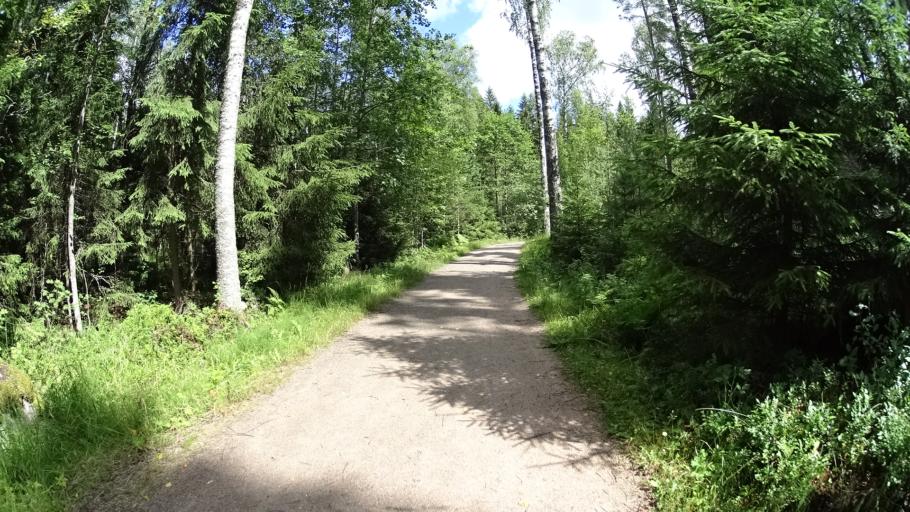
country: FI
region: Uusimaa
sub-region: Helsinki
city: Espoo
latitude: 60.3230
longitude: 24.6685
